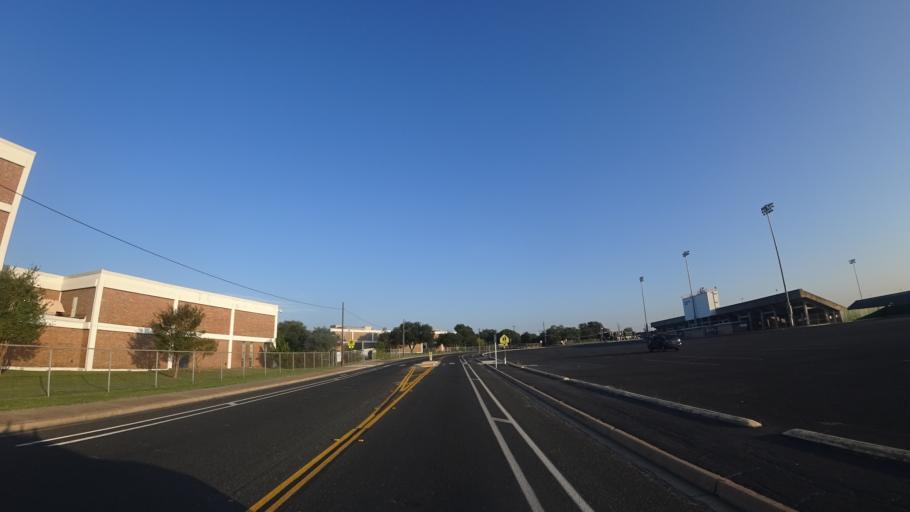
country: US
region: Texas
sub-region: Travis County
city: Austin
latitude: 30.3229
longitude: -97.6893
